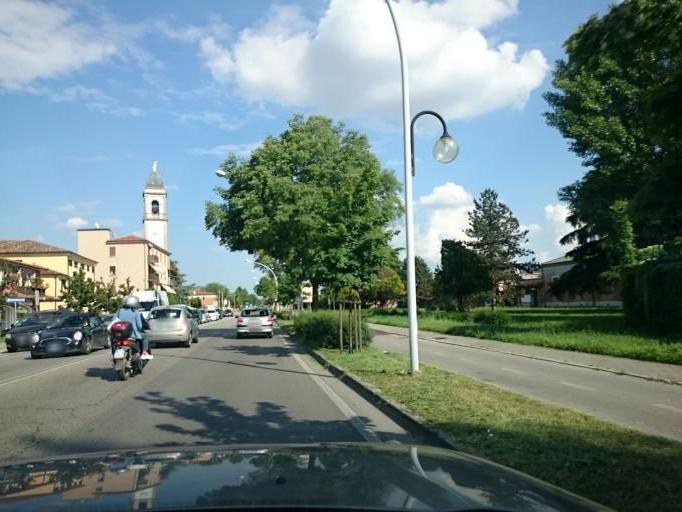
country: IT
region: Veneto
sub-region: Provincia di Padova
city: Caselle
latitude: 45.4149
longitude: 11.8342
